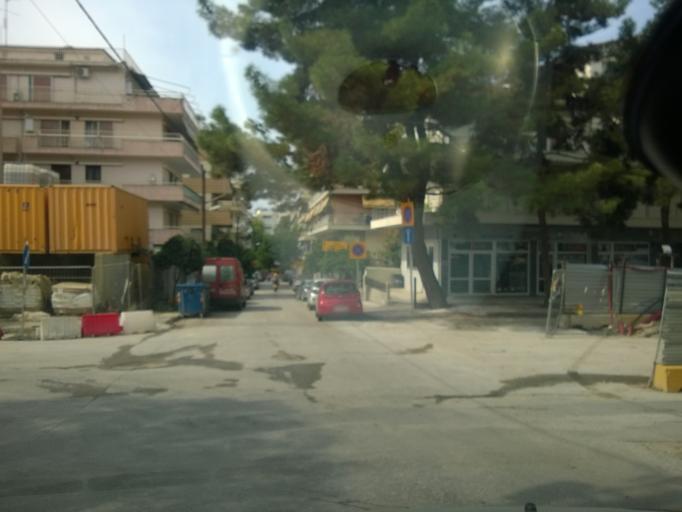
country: GR
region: Central Macedonia
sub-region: Nomos Thessalonikis
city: Kalamaria
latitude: 40.5944
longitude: 22.9611
